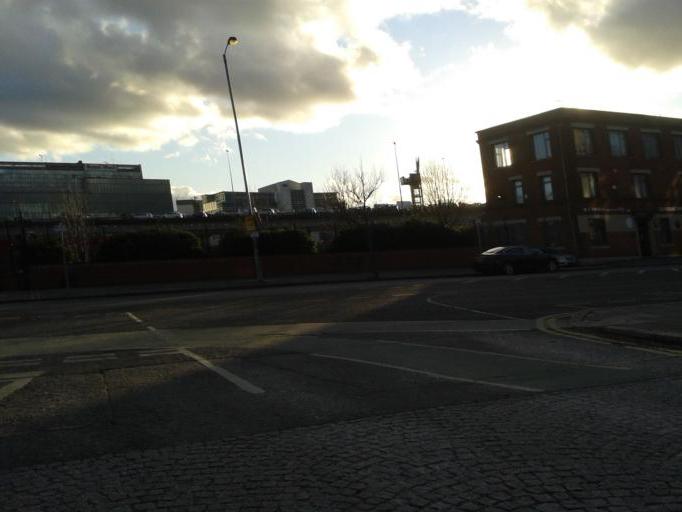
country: GB
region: Northern Ireland
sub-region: City of Belfast
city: Belfast
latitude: 54.6050
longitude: -5.9212
